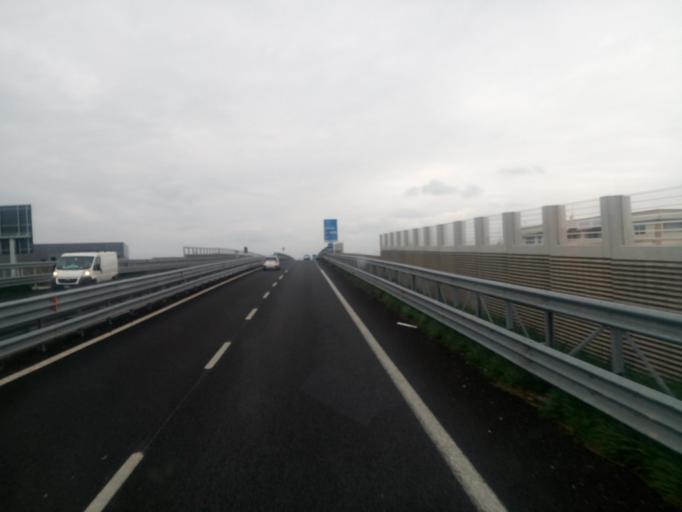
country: IT
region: Emilia-Romagna
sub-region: Forli-Cesena
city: Forli
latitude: 44.2226
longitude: 12.0841
